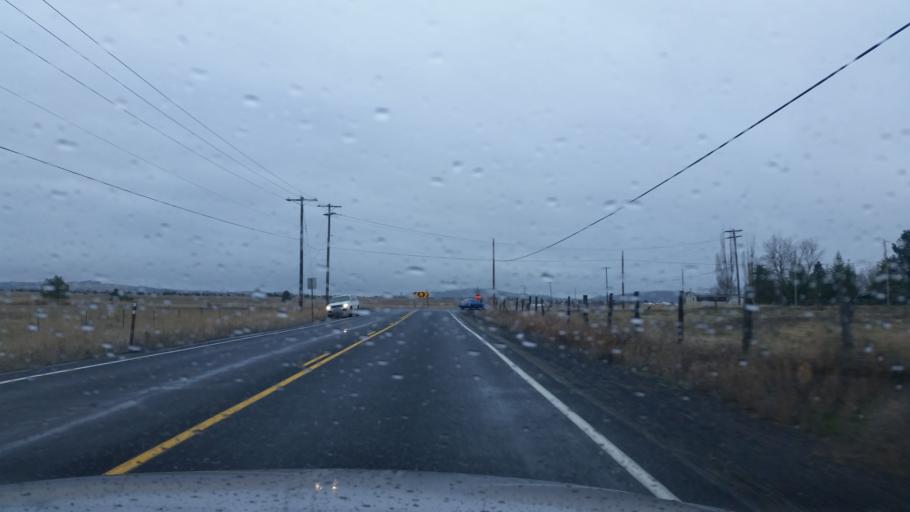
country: US
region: Washington
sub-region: Spokane County
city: Airway Heights
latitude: 47.6148
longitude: -117.6041
